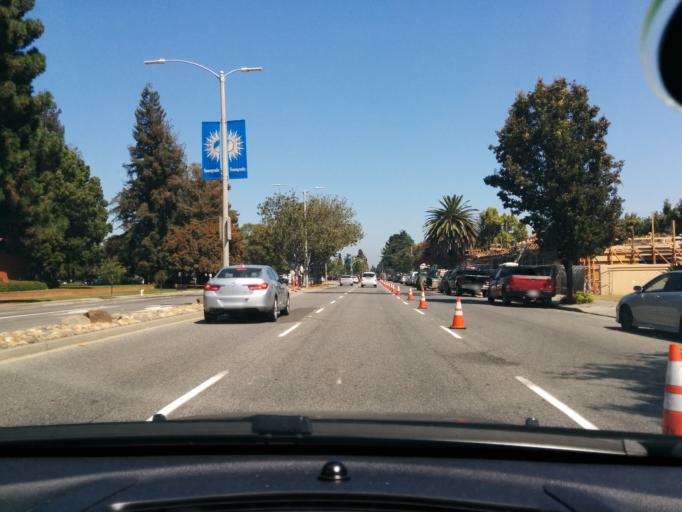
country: US
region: California
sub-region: Santa Clara County
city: Sunnyvale
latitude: 37.3702
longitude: -122.0366
